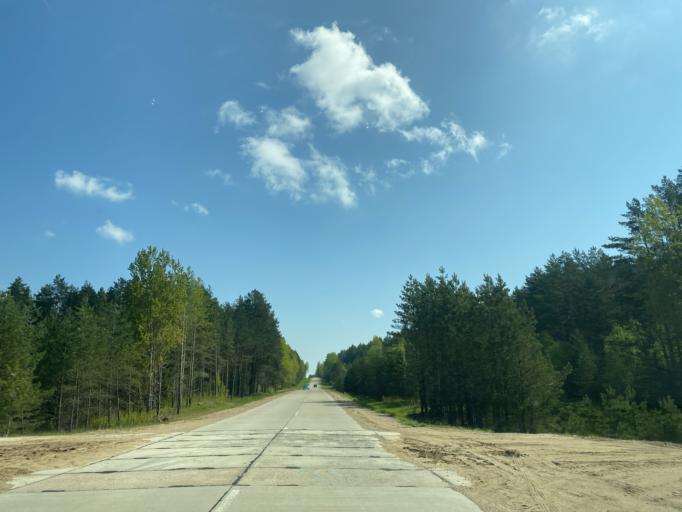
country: BY
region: Minsk
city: Horad Barysaw
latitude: 54.1602
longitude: 28.4888
